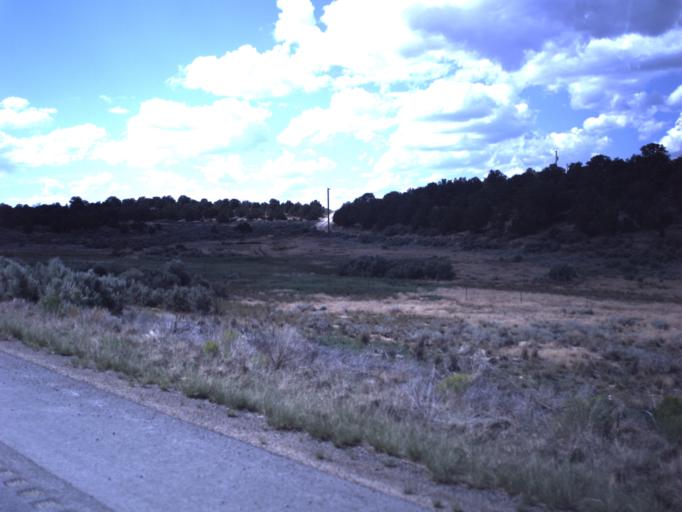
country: US
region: Utah
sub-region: Duchesne County
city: Duchesne
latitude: 40.1807
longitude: -110.6249
